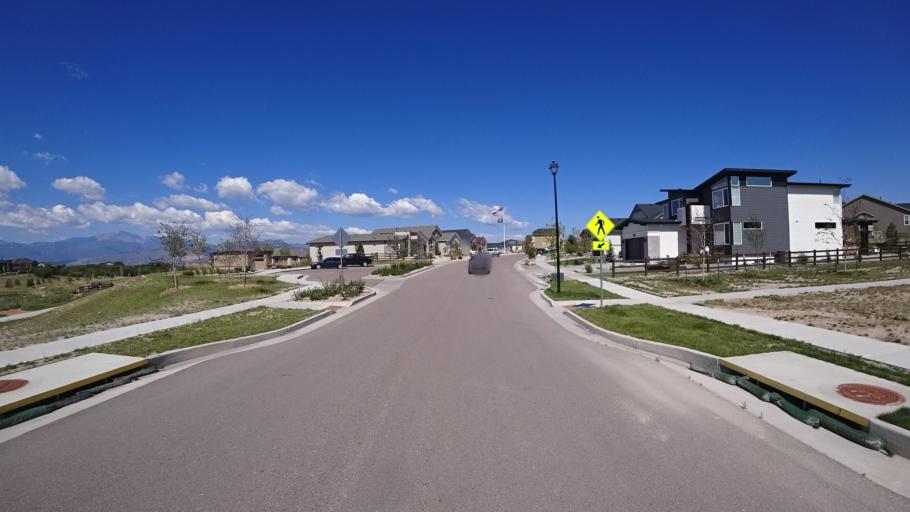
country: US
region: Colorado
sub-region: El Paso County
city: Black Forest
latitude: 38.9817
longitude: -104.7477
